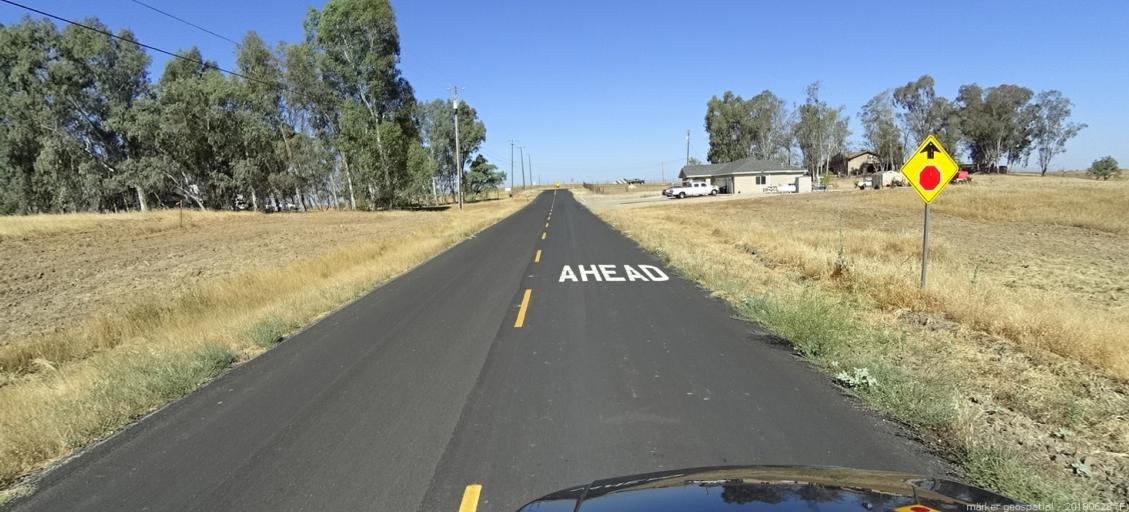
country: US
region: California
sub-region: Madera County
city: Bonadelle Ranchos-Madera Ranchos
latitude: 37.0058
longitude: -119.8916
